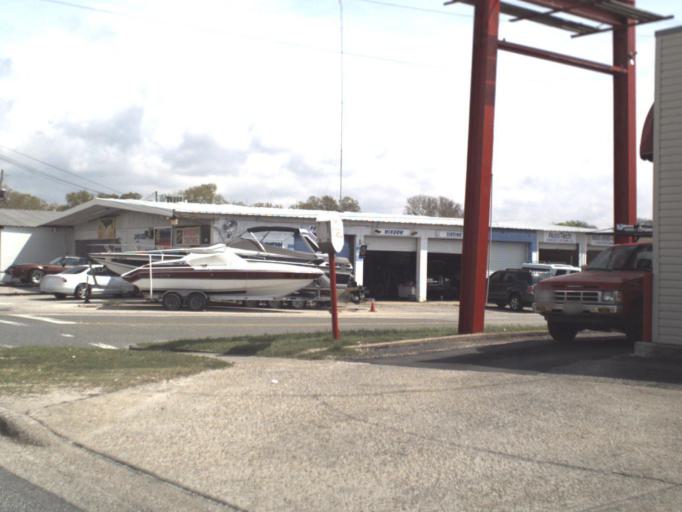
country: US
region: Florida
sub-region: Okaloosa County
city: Fort Walton Beach
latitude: 30.4211
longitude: -86.6136
